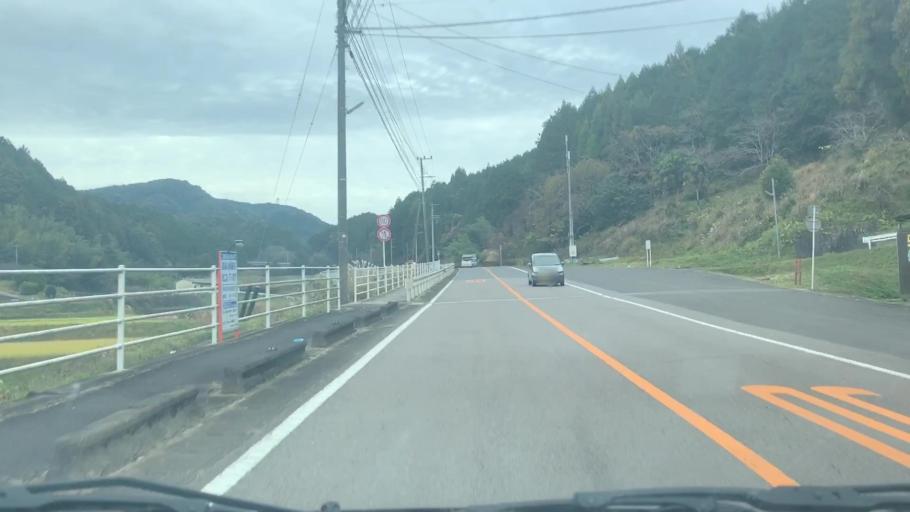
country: JP
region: Saga Prefecture
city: Ureshinomachi-shimojuku
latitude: 33.1538
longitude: 129.9728
